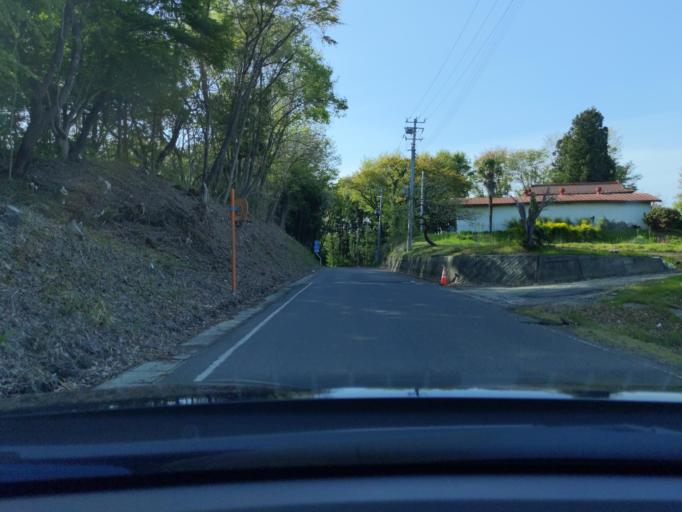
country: JP
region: Fukushima
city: Sukagawa
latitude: 37.2977
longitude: 140.4137
